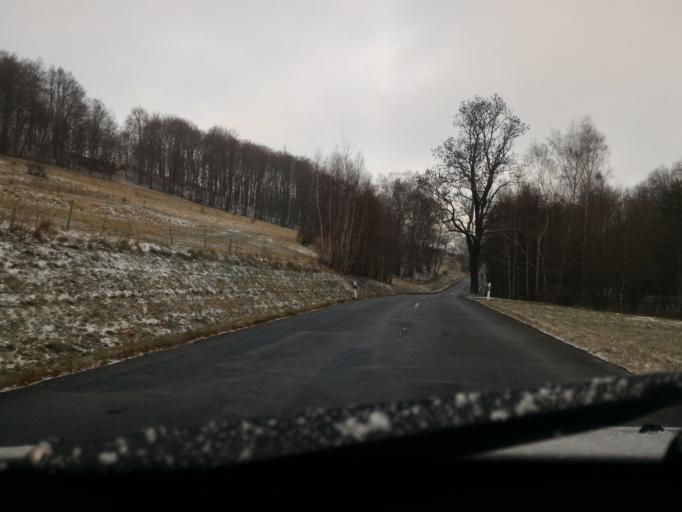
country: DE
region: Saxony
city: Grossschonau
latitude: 50.8629
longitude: 14.6598
